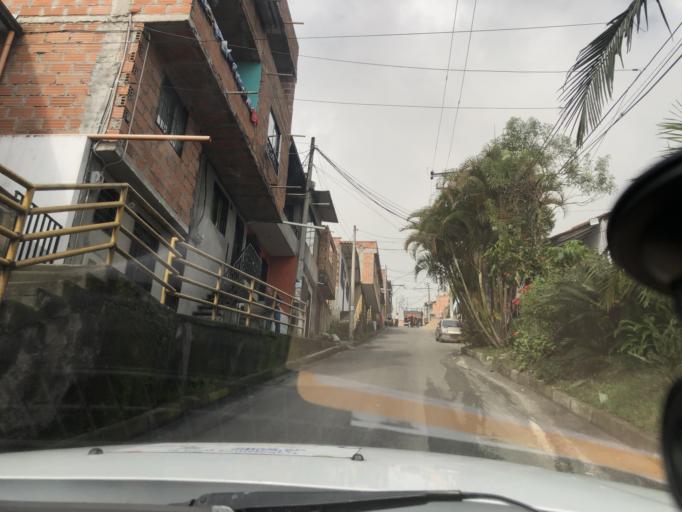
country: CO
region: Antioquia
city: Bello
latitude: 6.3149
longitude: -75.5859
